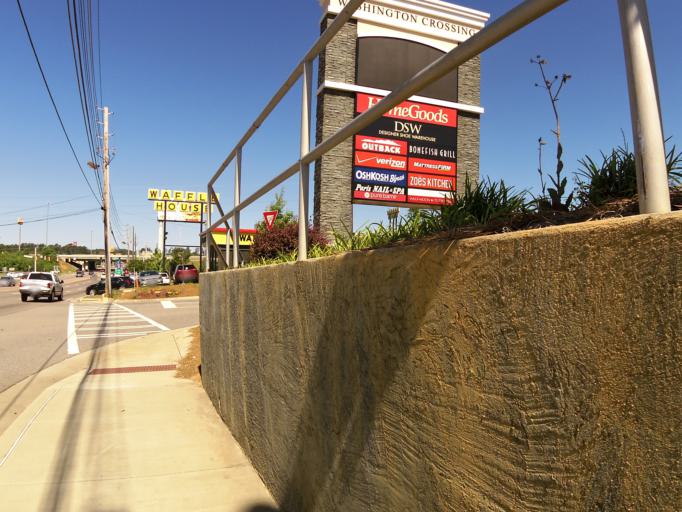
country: US
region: Georgia
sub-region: Columbia County
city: Martinez
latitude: 33.5117
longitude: -82.0397
